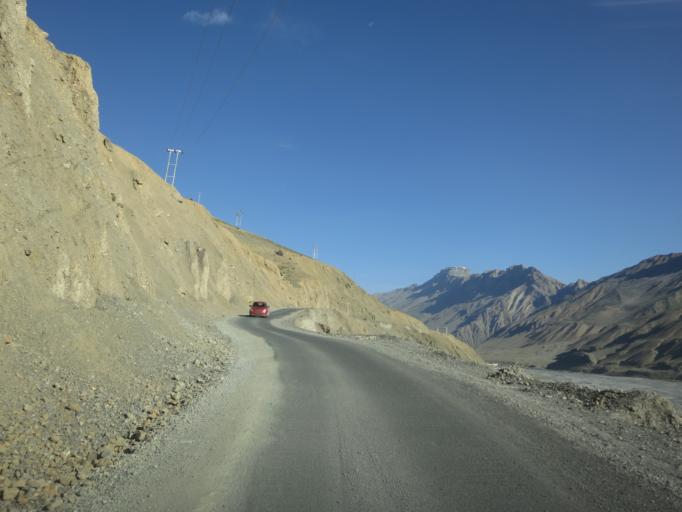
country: IN
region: Himachal Pradesh
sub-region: Shimla
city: Sarahan
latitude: 32.2405
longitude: 78.0593
